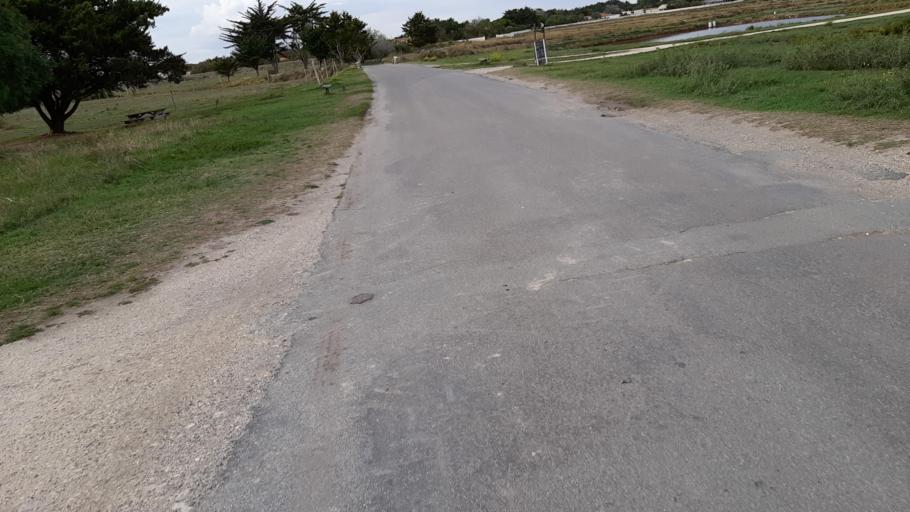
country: FR
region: Poitou-Charentes
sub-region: Departement de la Charente-Maritime
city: Boyard-Ville
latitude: 46.0136
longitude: -1.1730
